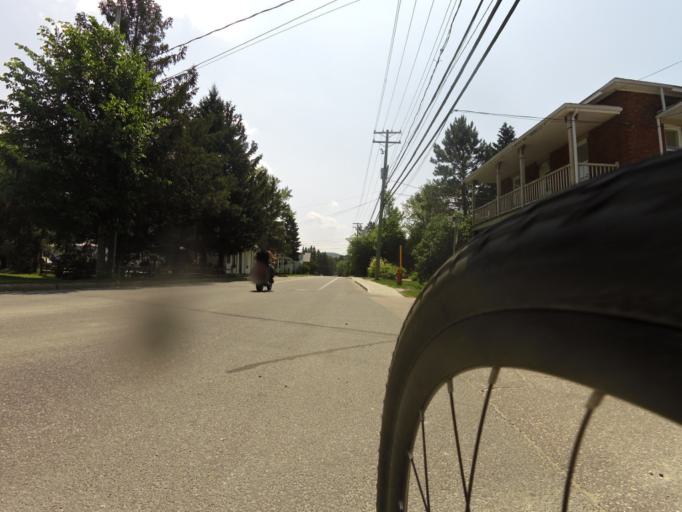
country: CA
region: Quebec
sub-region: Laurentides
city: Mont-Tremblant
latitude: 46.1302
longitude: -74.5907
